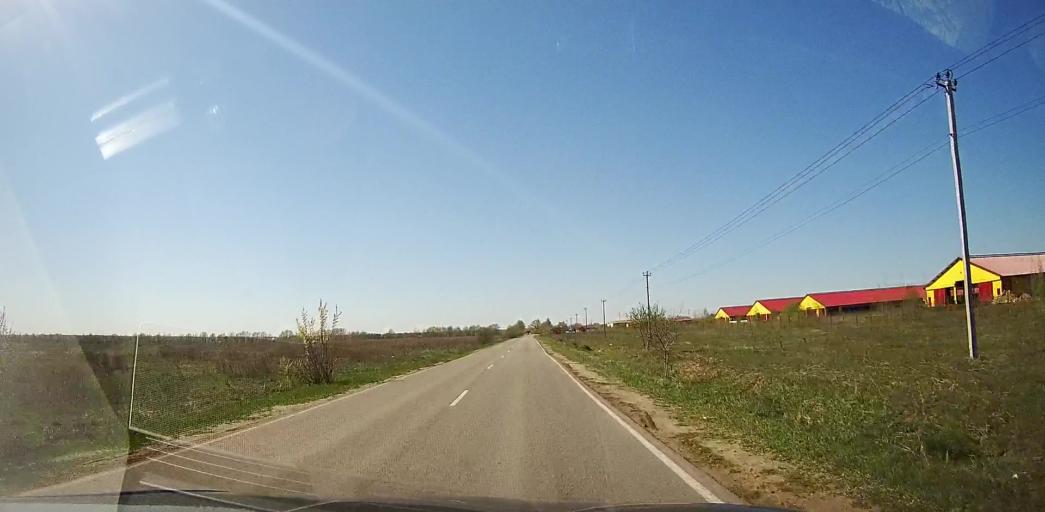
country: RU
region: Moskovskaya
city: Bronnitsy
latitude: 55.4762
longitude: 38.2487
